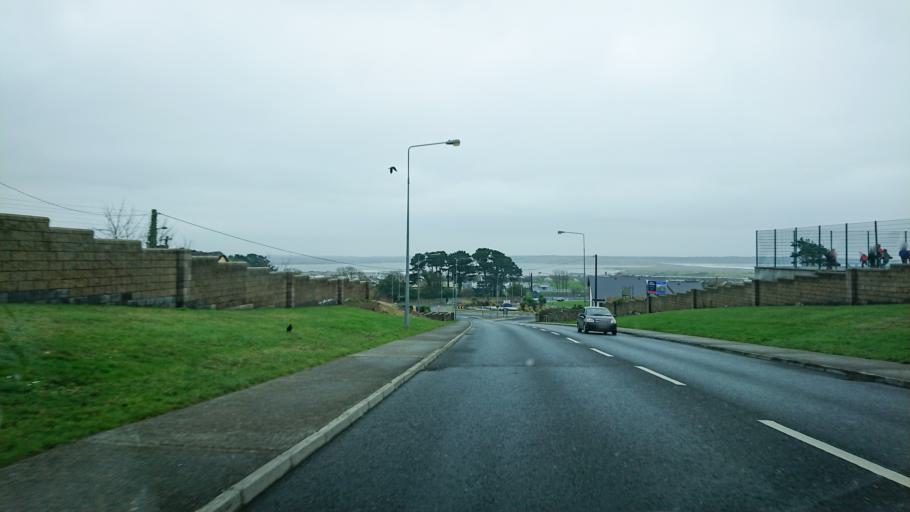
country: IE
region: Munster
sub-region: Waterford
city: Tra Mhor
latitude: 52.1694
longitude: -7.1462
